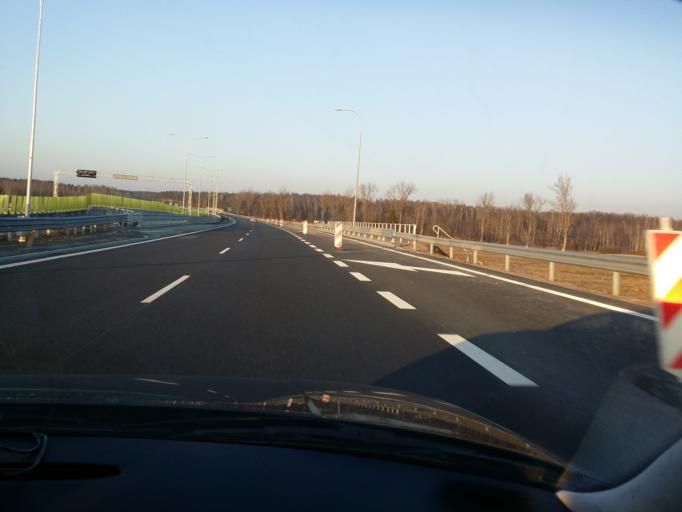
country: PL
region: Swietokrzyskie
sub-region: Powiat skarzyski
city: Skarzysko-Kamienna
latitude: 51.1621
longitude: 20.8562
